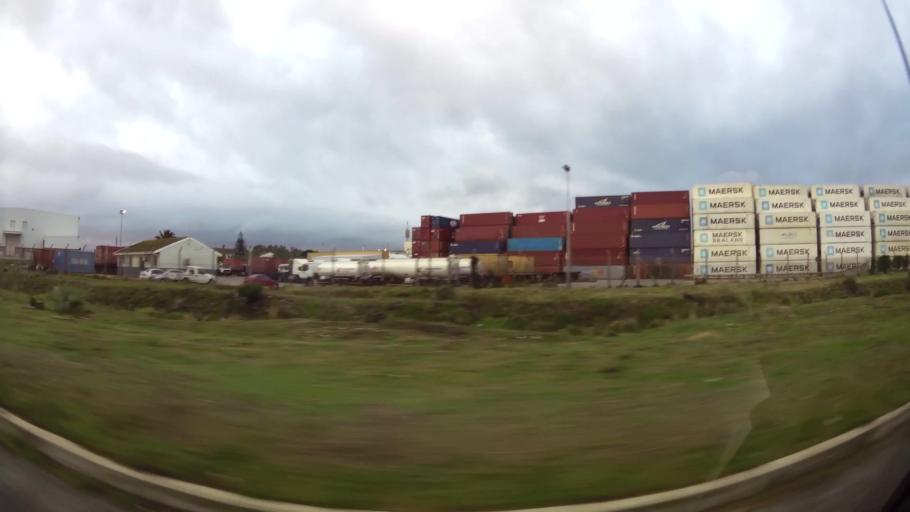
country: ZA
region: Eastern Cape
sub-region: Nelson Mandela Bay Metropolitan Municipality
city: Port Elizabeth
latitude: -33.9244
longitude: 25.5993
